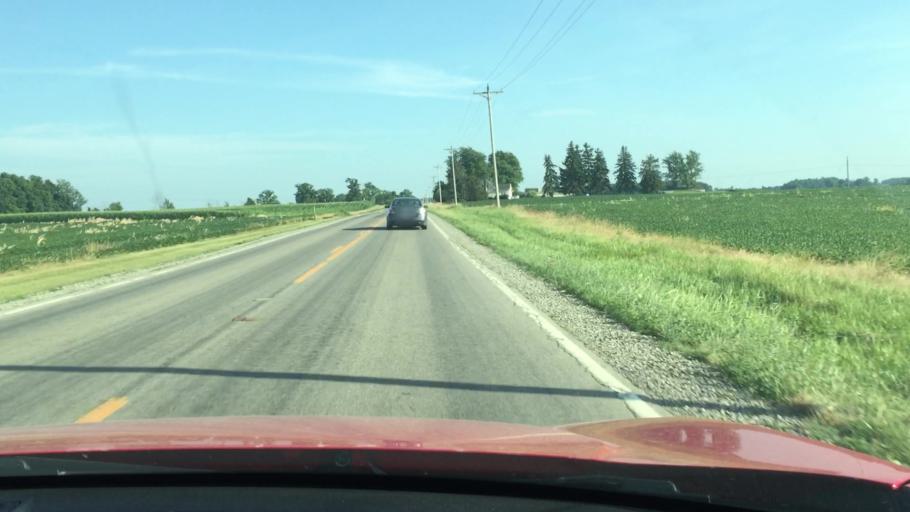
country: US
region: Ohio
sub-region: Hardin County
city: Ada
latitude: 40.6729
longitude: -83.8558
